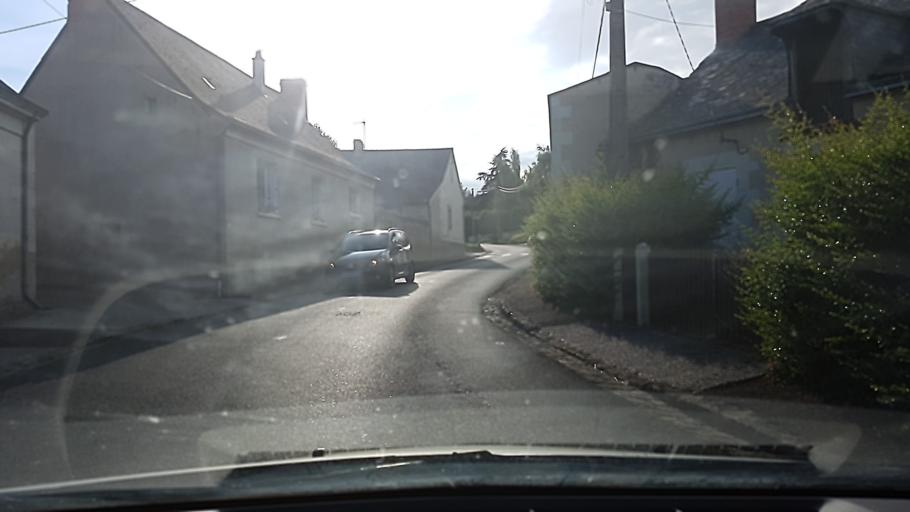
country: FR
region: Pays de la Loire
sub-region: Departement de Maine-et-Loire
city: Maze
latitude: 47.5015
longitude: -0.2504
